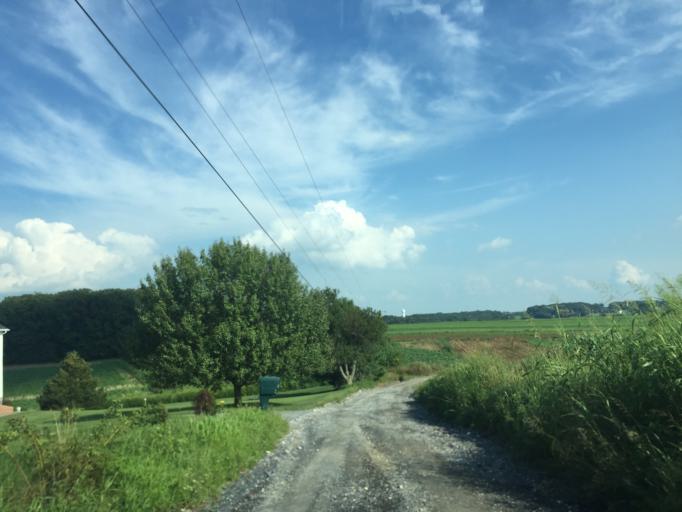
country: US
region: Maryland
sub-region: Carroll County
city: Manchester
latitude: 39.6295
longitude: -76.8822
